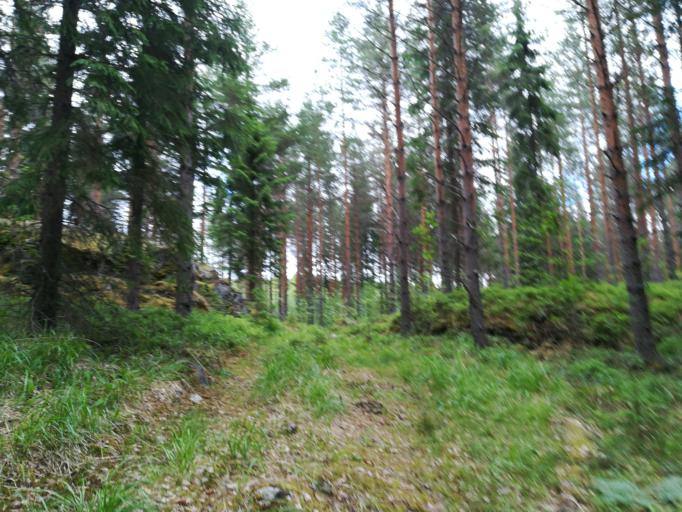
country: FI
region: South Karelia
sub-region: Lappeenranta
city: Savitaipale
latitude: 61.3039
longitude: 27.6160
